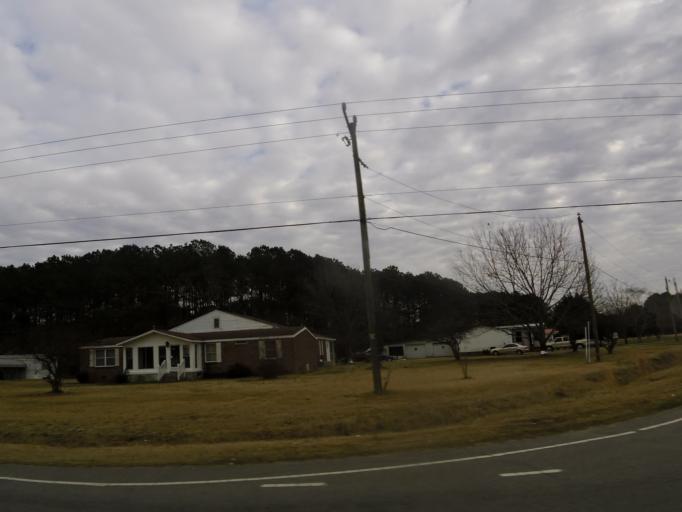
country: US
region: North Carolina
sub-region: Northampton County
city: Jackson
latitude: 36.3038
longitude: -77.2668
